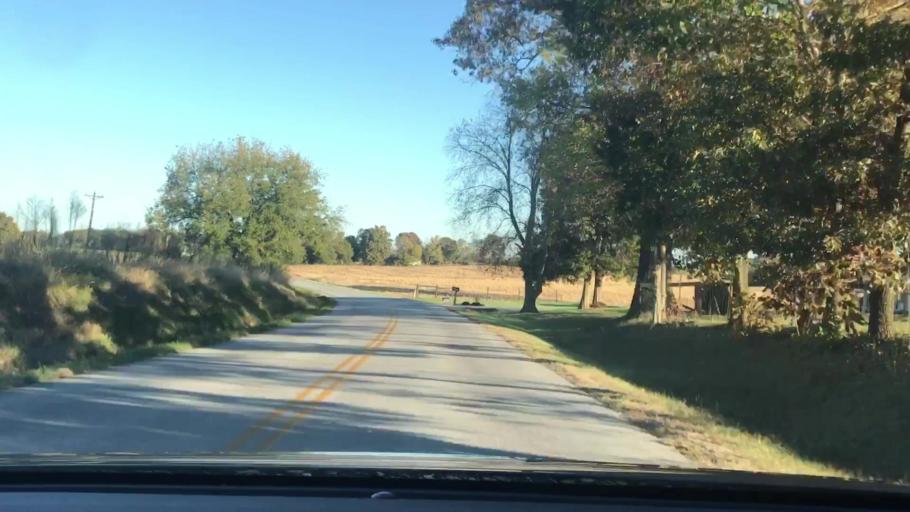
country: US
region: Kentucky
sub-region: Simpson County
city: Franklin
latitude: 36.7892
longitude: -86.6261
